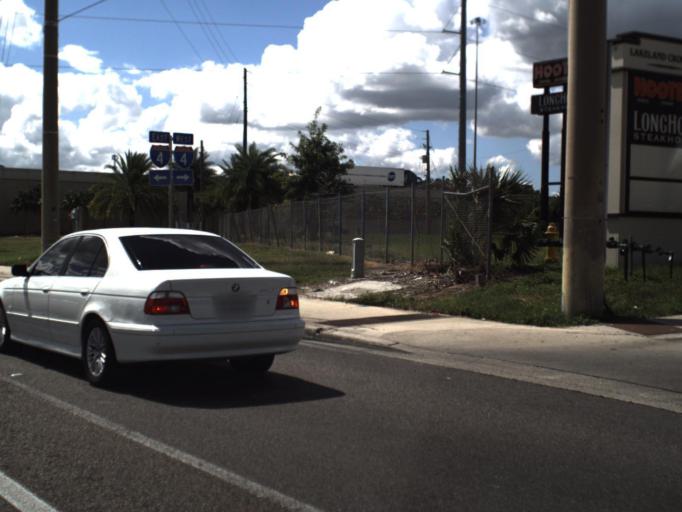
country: US
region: Florida
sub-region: Polk County
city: Gibsonia
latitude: 28.0862
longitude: -81.9716
